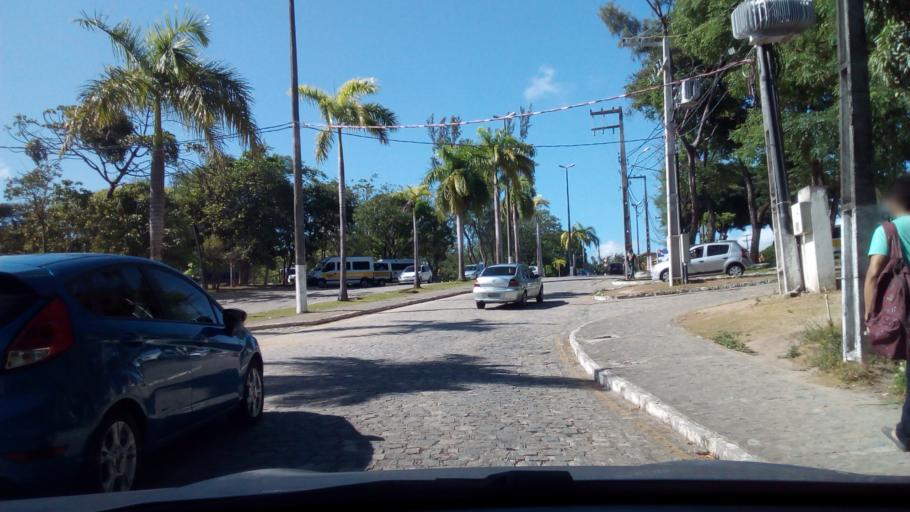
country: BR
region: Paraiba
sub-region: Joao Pessoa
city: Joao Pessoa
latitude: -7.1577
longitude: -34.8528
